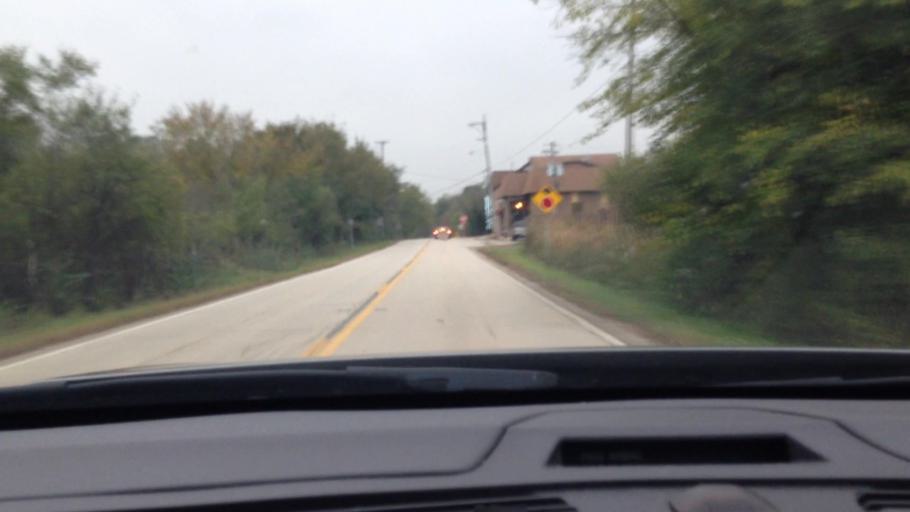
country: US
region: Illinois
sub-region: Cook County
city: Barrington Hills
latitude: 42.0945
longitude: -88.1946
